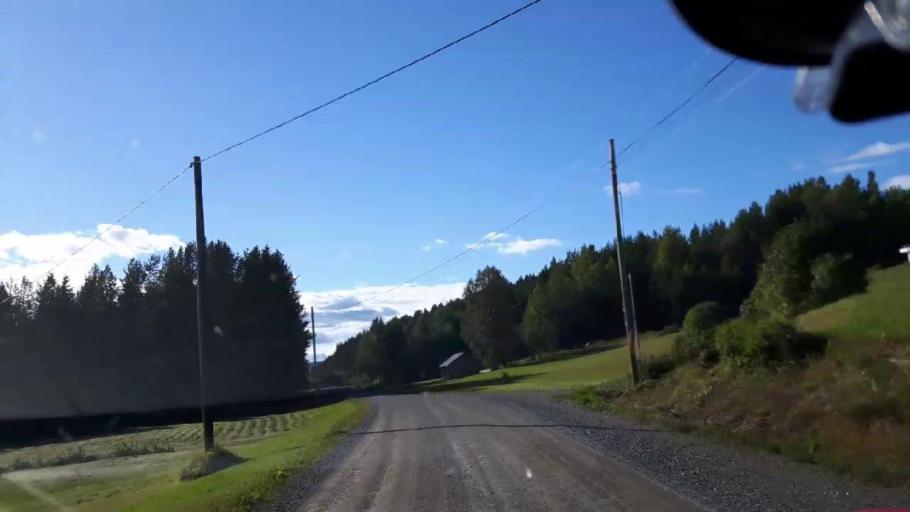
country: SE
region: Jaemtland
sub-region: Ragunda Kommun
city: Hammarstrand
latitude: 63.4875
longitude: 16.0940
